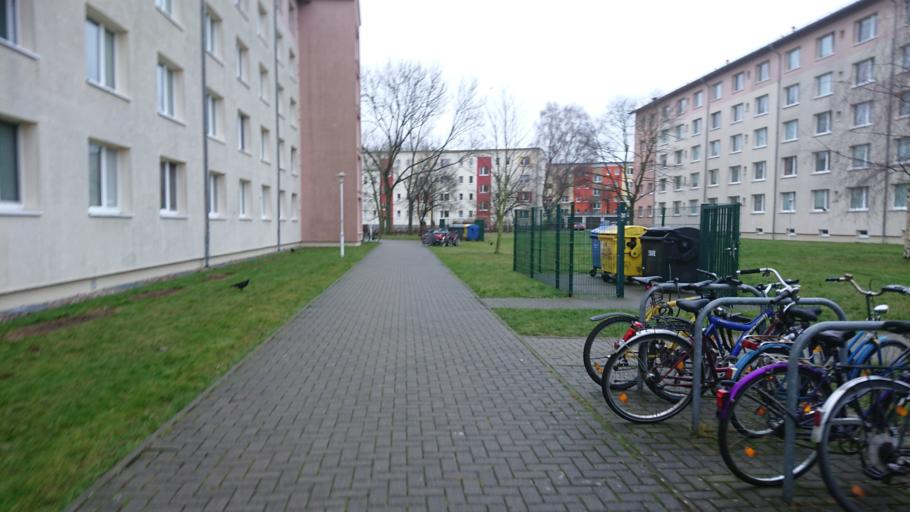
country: DE
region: Mecklenburg-Vorpommern
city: Rostock
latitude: 54.0757
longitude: 12.1124
